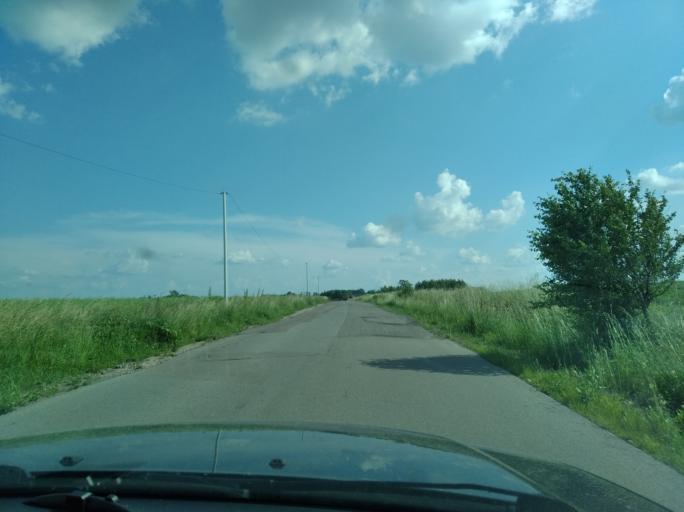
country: PL
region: Subcarpathian Voivodeship
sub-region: Powiat jaroslawski
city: Ostrow
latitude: 49.9337
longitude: 22.7400
